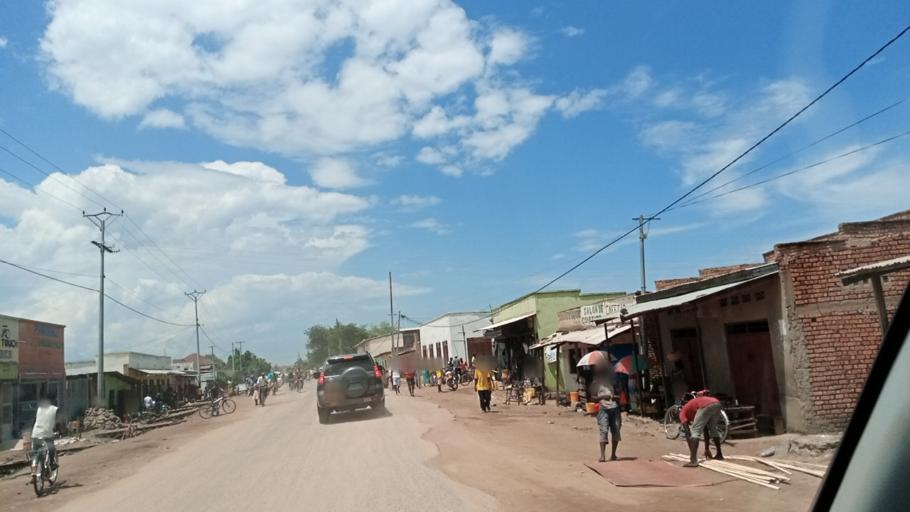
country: BI
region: Bujumbura Mairie
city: Bujumbura
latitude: -3.4281
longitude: 29.3548
